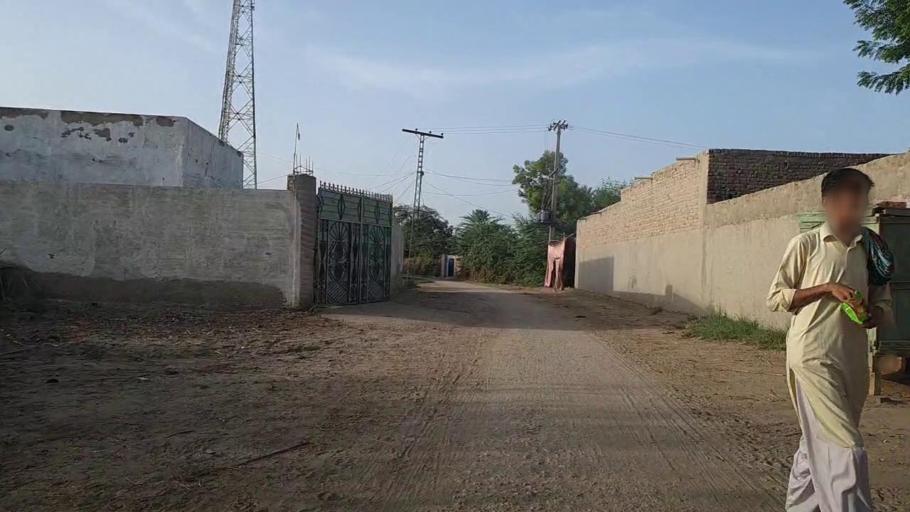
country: PK
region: Sindh
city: Bhiria
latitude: 26.9100
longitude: 68.2637
